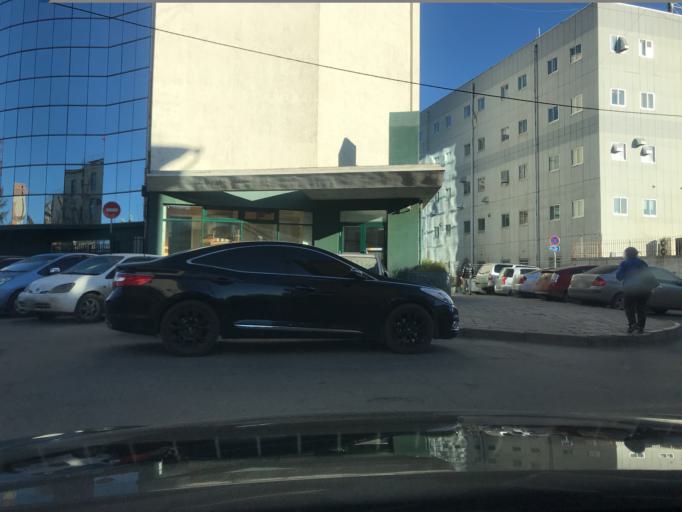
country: MN
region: Ulaanbaatar
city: Ulaanbaatar
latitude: 47.9181
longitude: 106.9124
